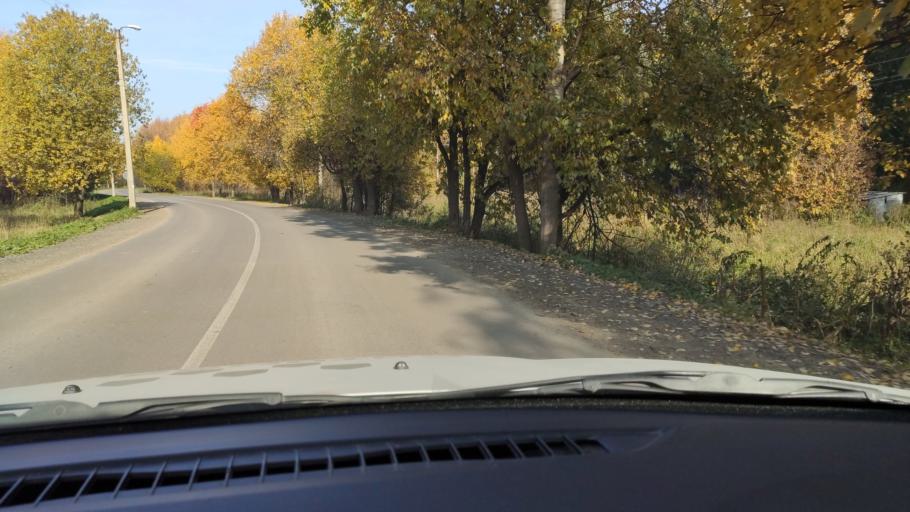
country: RU
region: Perm
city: Sylva
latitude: 58.0317
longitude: 56.7408
